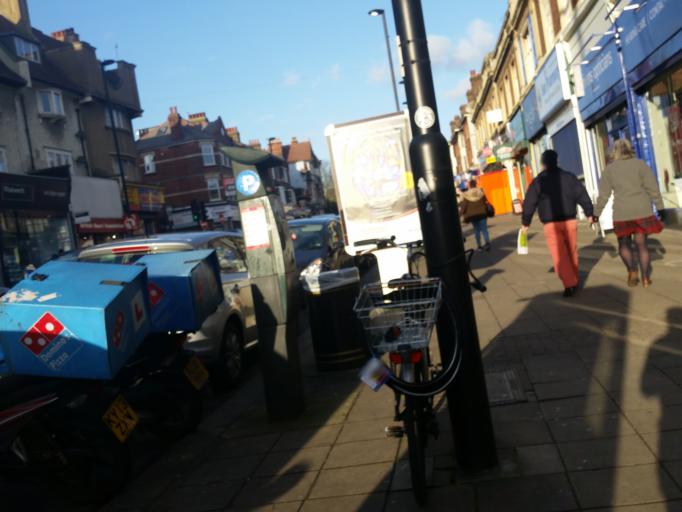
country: GB
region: England
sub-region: Greater London
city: Wood Green
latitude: 51.6194
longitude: -0.1069
